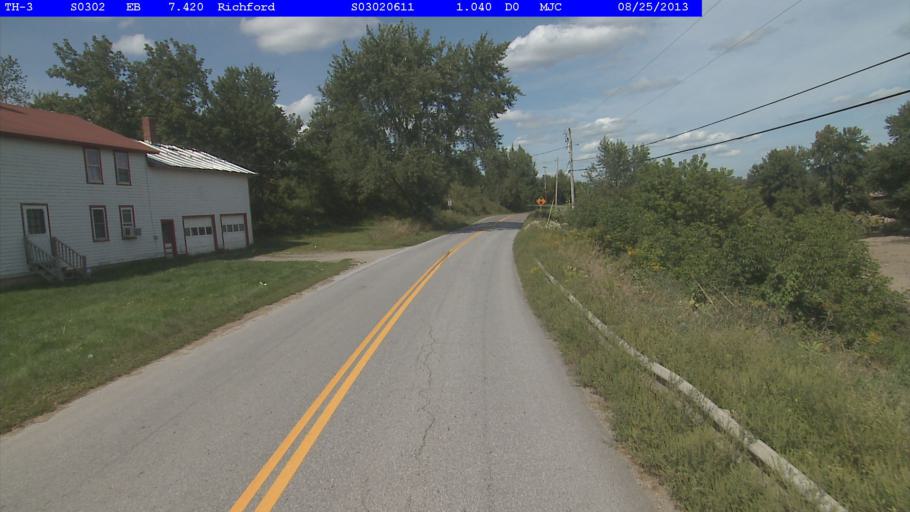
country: US
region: Vermont
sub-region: Franklin County
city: Richford
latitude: 44.9997
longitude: -72.6805
